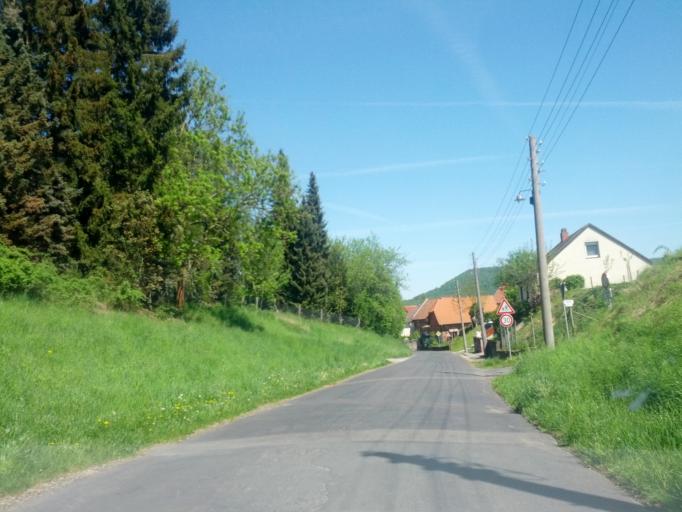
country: DE
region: Hesse
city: Wanfried
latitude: 51.1334
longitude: 10.1723
